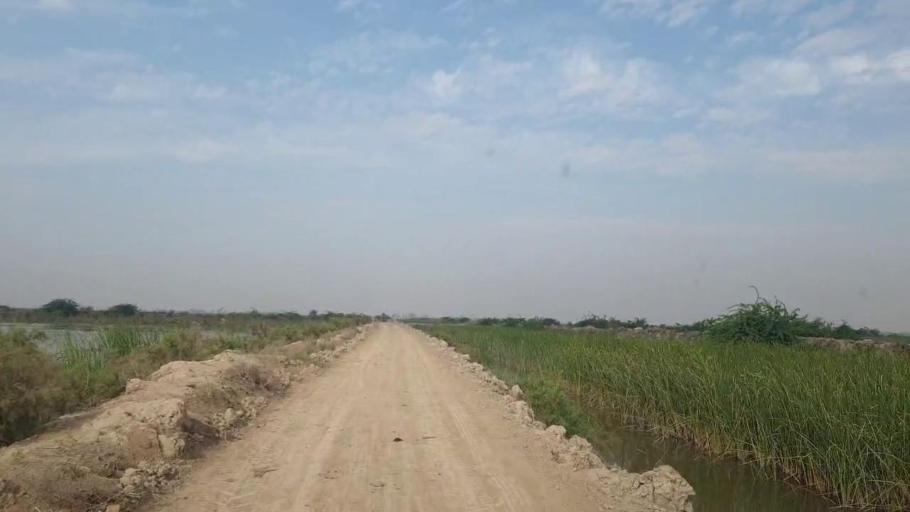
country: PK
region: Sindh
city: Tando Bago
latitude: 24.8664
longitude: 68.9858
